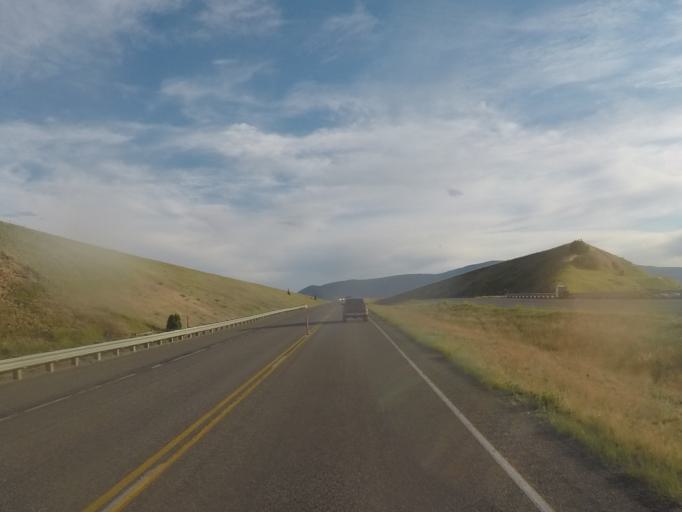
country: US
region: Montana
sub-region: Park County
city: Livingston
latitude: 45.6753
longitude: -110.5154
